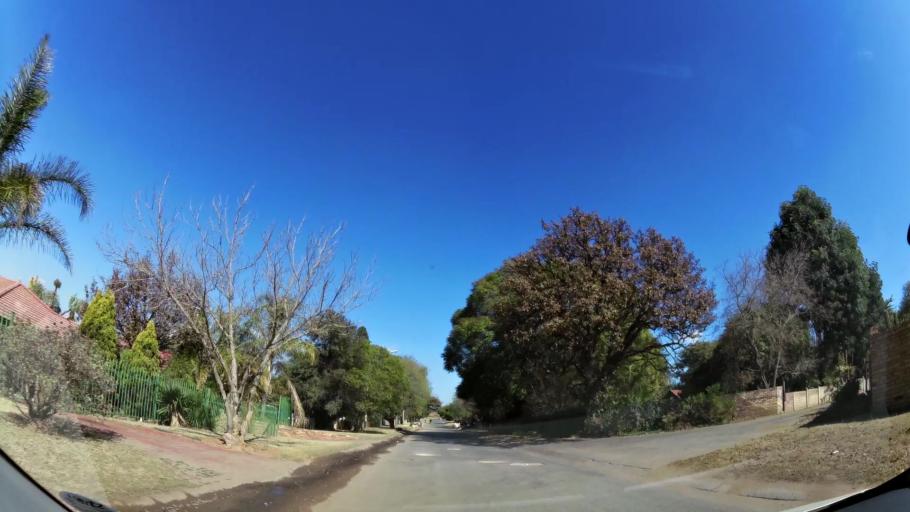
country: ZA
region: Mpumalanga
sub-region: Nkangala District Municipality
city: Witbank
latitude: -25.8475
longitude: 29.2434
